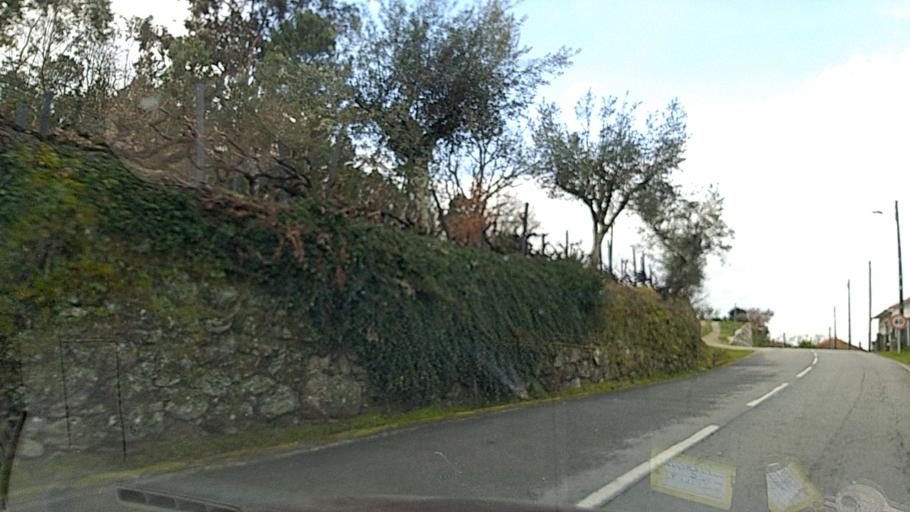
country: PT
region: Guarda
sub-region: Fornos de Algodres
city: Fornos de Algodres
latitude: 40.6632
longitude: -7.6238
